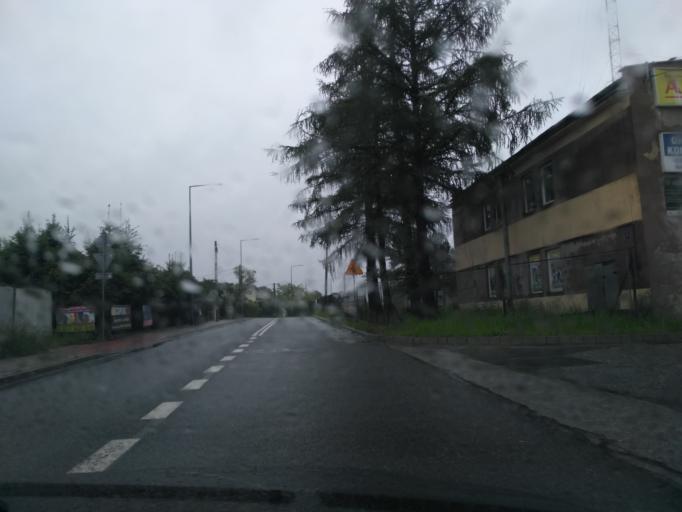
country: PL
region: Lesser Poland Voivodeship
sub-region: Powiat gorlicki
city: Gorlice
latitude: 49.6791
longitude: 21.1696
